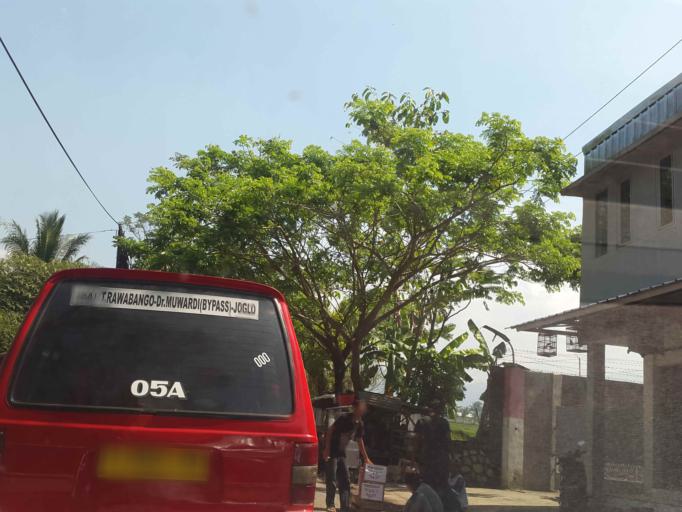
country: ID
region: West Java
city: Ciranjang-hilir
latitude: -6.8276
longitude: 107.1142
